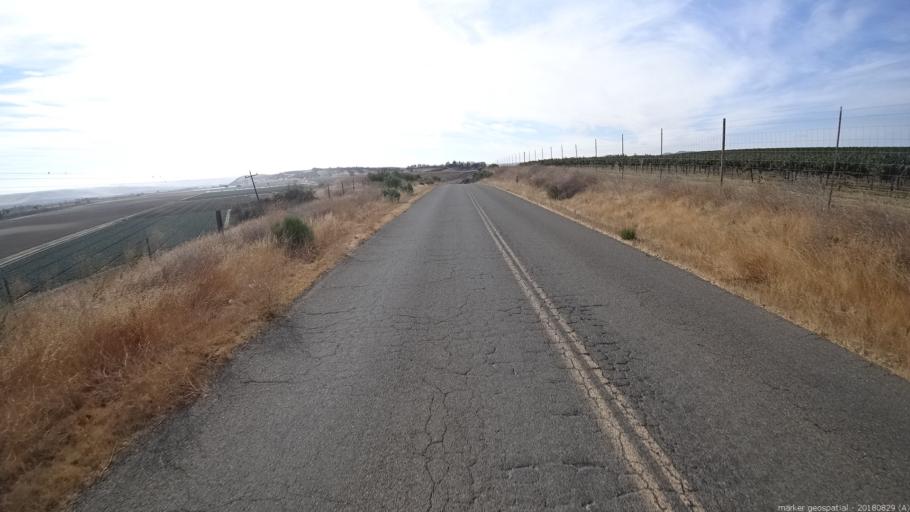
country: US
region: California
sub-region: Monterey County
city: King City
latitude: 36.0926
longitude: -121.0111
